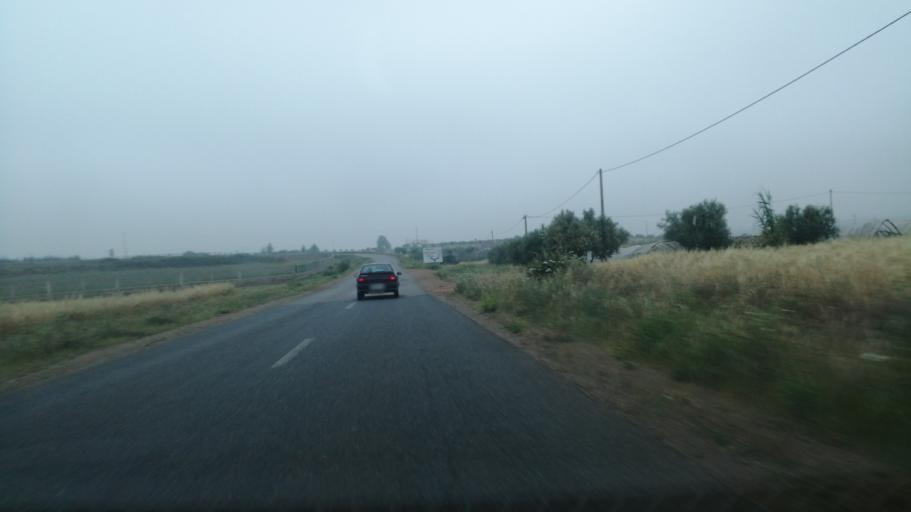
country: MA
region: Rabat-Sale-Zemmour-Zaer
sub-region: Khemisset
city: Tiflet
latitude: 33.7407
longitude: -6.2698
